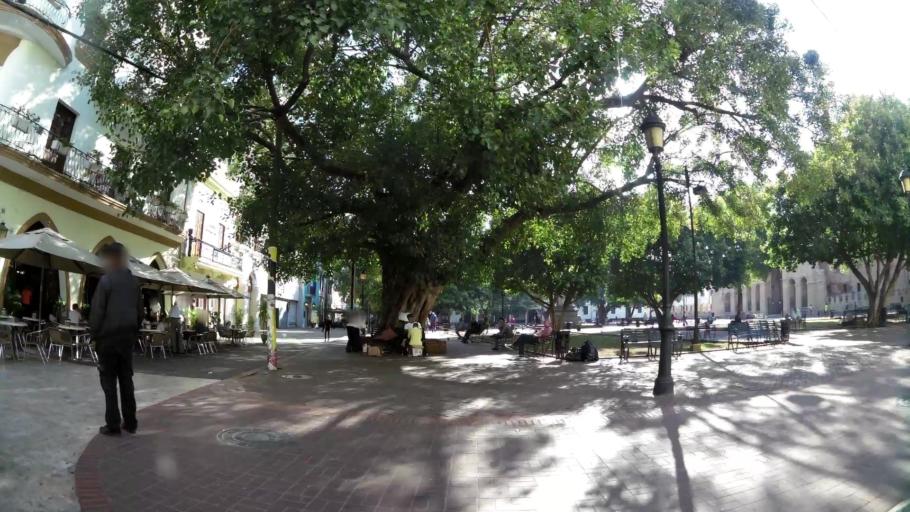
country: DO
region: Nacional
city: Ciudad Nueva
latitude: 18.4735
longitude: -69.8845
